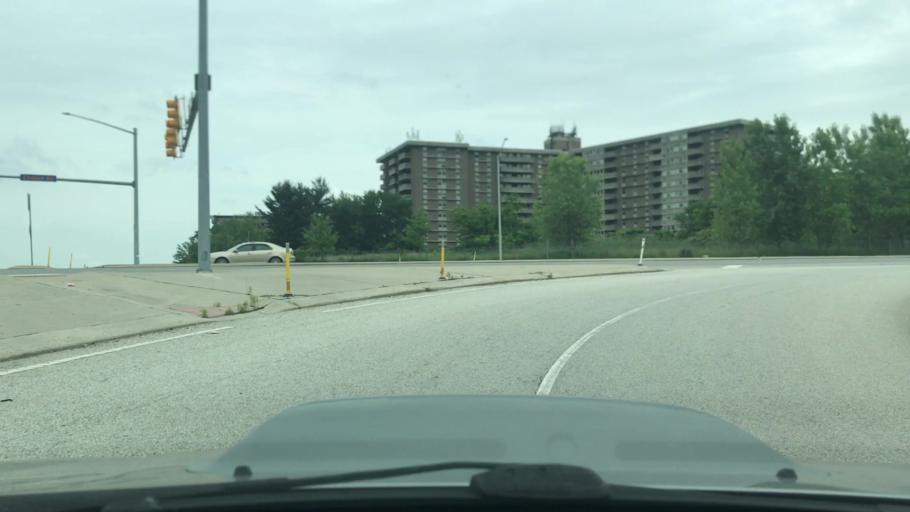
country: US
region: Pennsylvania
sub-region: Montgomery County
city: Wyncote
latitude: 40.0871
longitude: -75.1652
